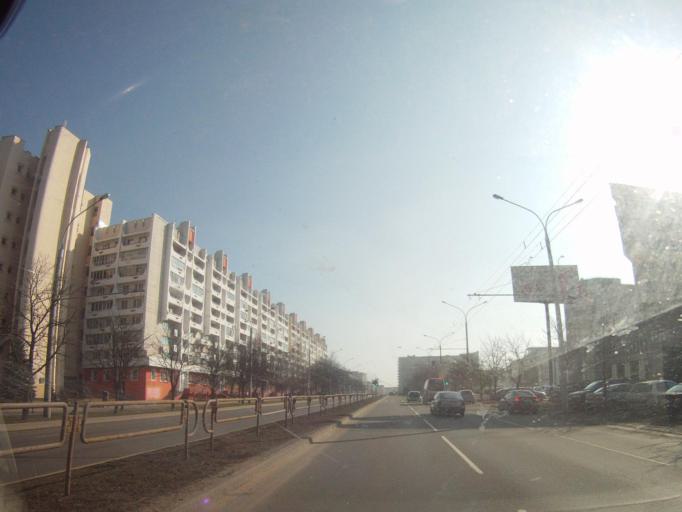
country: BY
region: Minsk
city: Minsk
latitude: 53.9277
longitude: 27.5885
